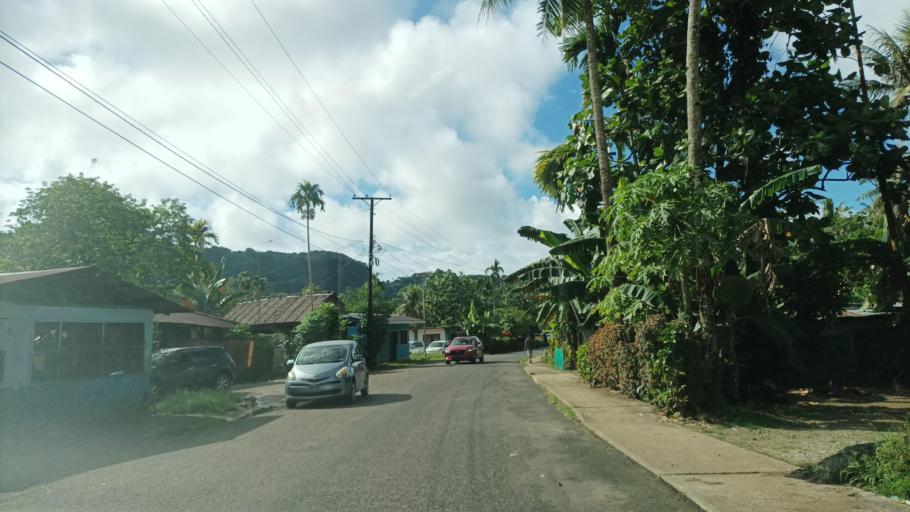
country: FM
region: Pohnpei
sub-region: Kolonia Municipality
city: Kolonia Town
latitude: 6.9620
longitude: 158.2056
